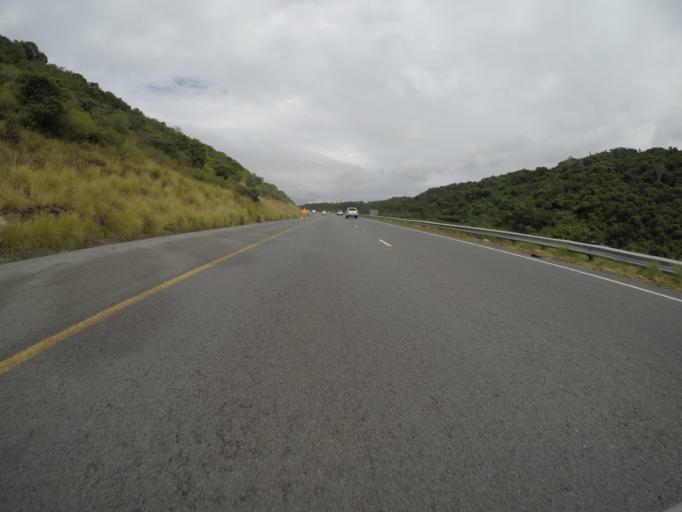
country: ZA
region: Eastern Cape
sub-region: Buffalo City Metropolitan Municipality
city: East London
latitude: -32.9688
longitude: 27.9141
